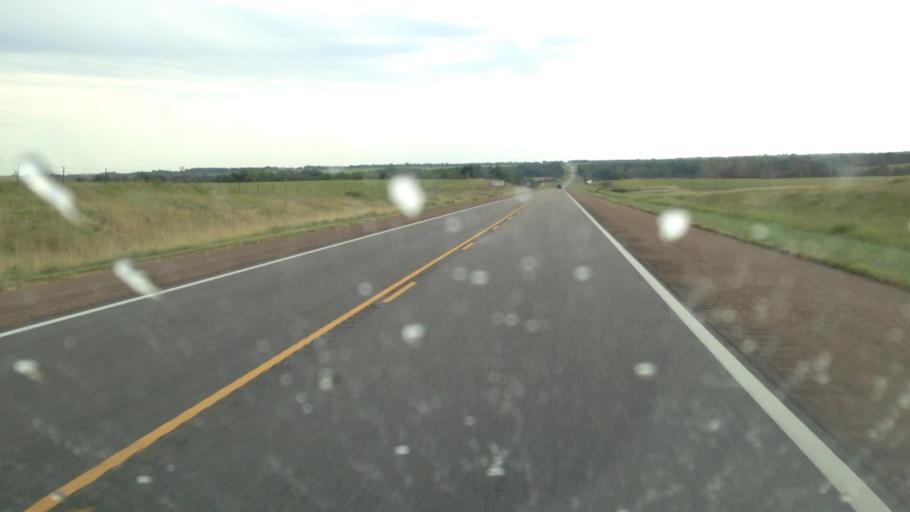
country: US
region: Kansas
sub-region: Coffey County
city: Burlington
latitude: 38.0445
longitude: -95.7391
